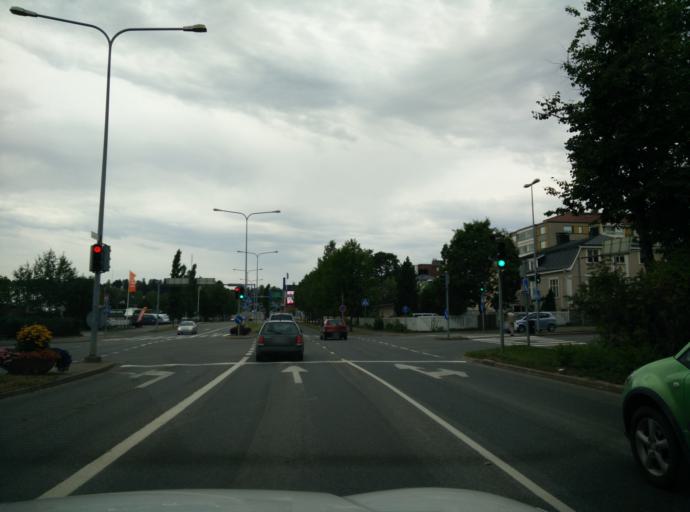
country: FI
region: Haeme
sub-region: Haemeenlinna
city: Haemeenlinna
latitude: 60.9941
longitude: 24.4650
